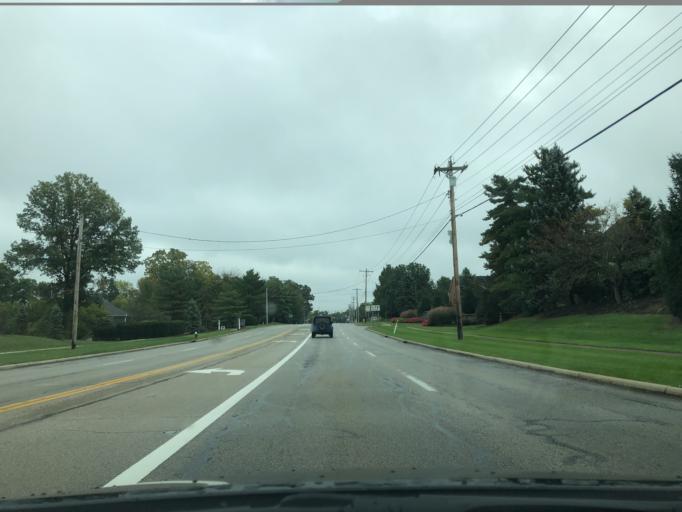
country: US
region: Ohio
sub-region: Hamilton County
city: Sixteen Mile Stand
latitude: 39.2750
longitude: -84.3329
